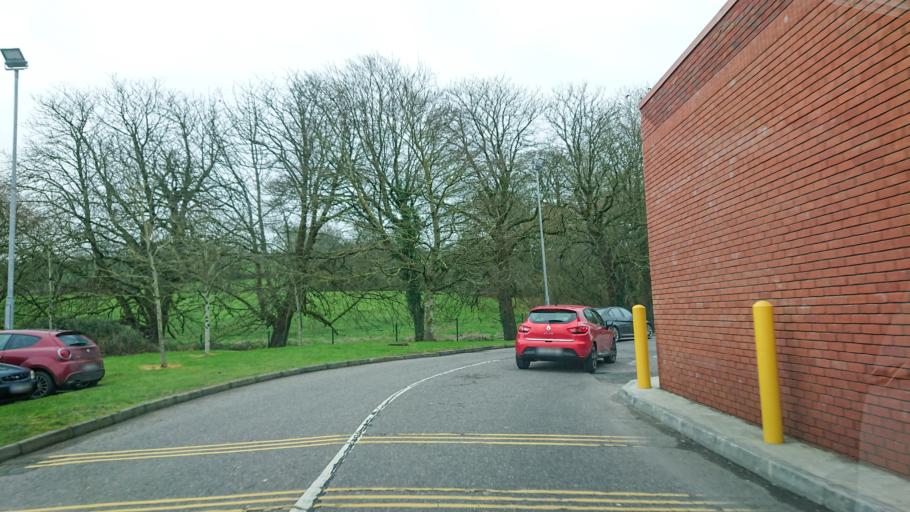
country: IE
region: Munster
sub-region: County Cork
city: Cork
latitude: 51.8736
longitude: -8.5197
